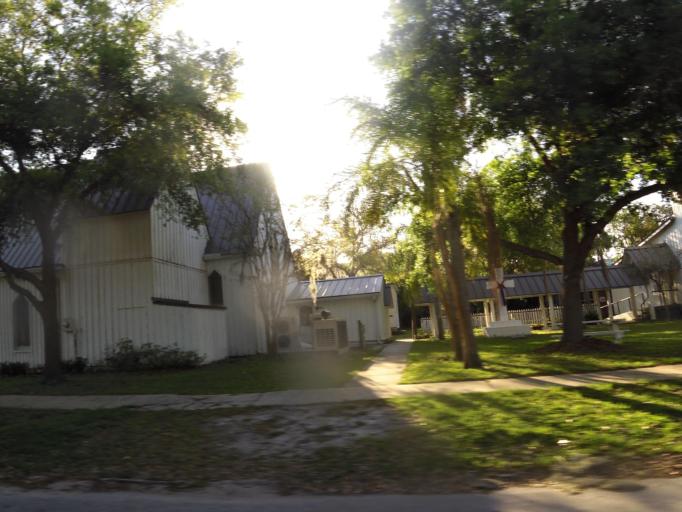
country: US
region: Florida
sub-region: Putnam County
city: Palatka
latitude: 29.6489
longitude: -81.6294
